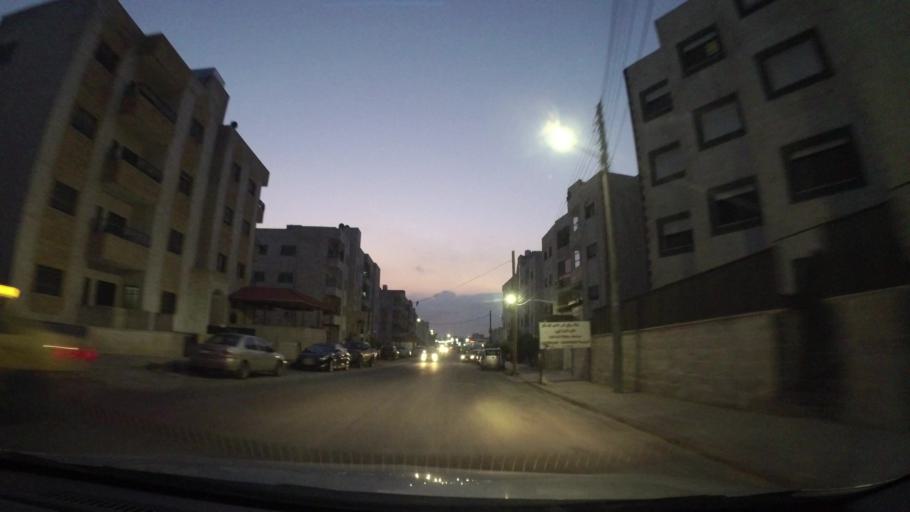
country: JO
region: Amman
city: Al Bunayyat ash Shamaliyah
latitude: 31.8949
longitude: 35.9200
